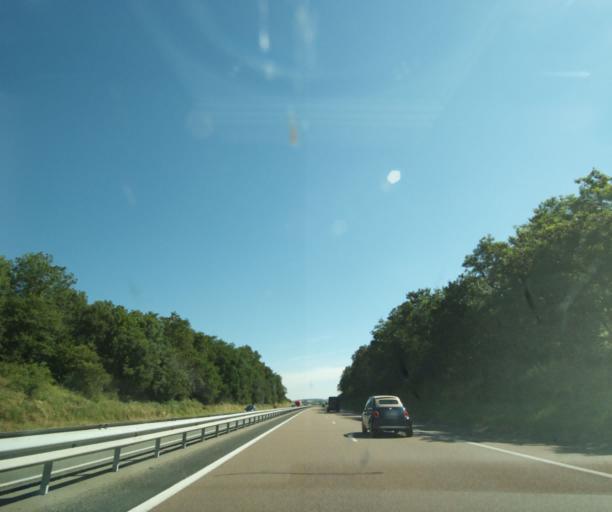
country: FR
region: Champagne-Ardenne
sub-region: Departement de la Haute-Marne
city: Saulxures
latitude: 48.0701
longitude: 5.5949
